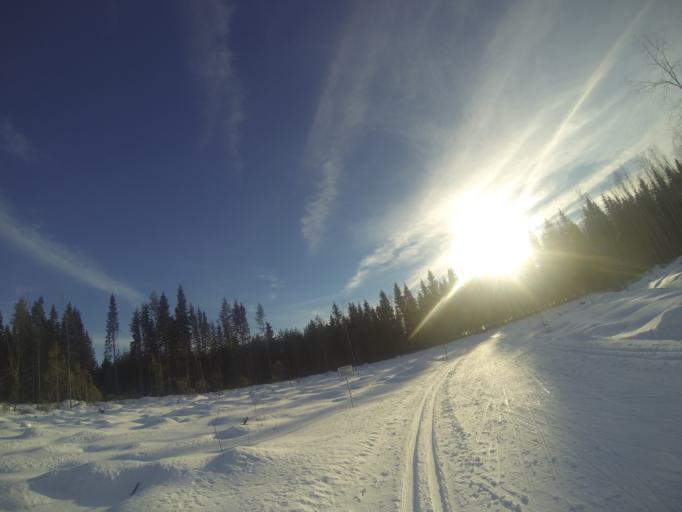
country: FI
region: Southern Savonia
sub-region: Savonlinna
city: Savonlinna
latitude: 61.9352
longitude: 28.9121
